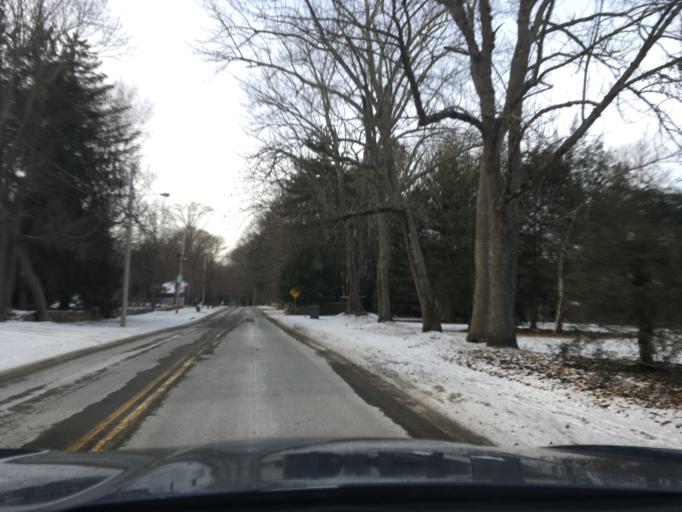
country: US
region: Rhode Island
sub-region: Kent County
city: East Greenwich
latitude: 41.6556
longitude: -71.4647
